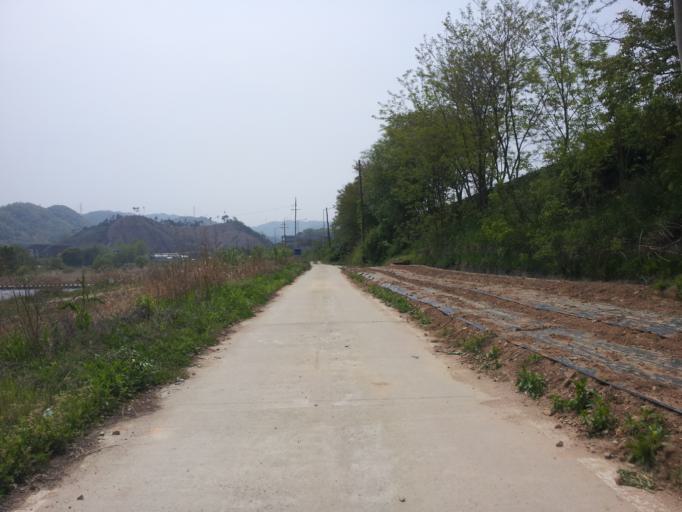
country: KR
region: Daejeon
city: Daejeon
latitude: 36.2608
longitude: 127.2850
